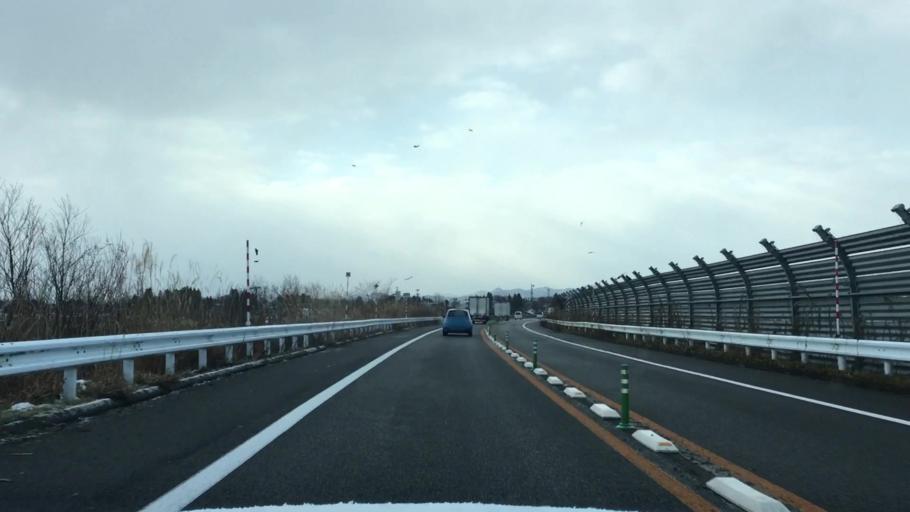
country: JP
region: Akita
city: Odate
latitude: 40.2844
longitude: 140.5408
